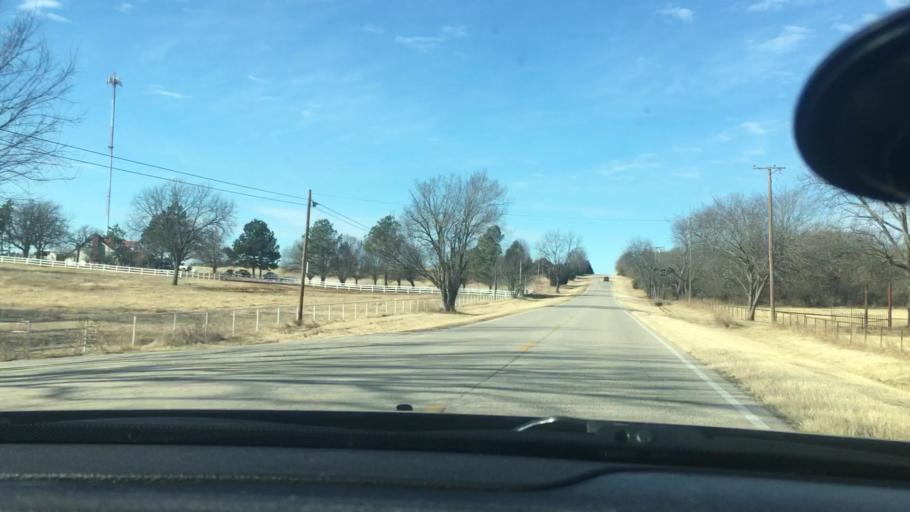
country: US
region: Oklahoma
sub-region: Garvin County
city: Stratford
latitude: 34.9860
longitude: -96.9663
